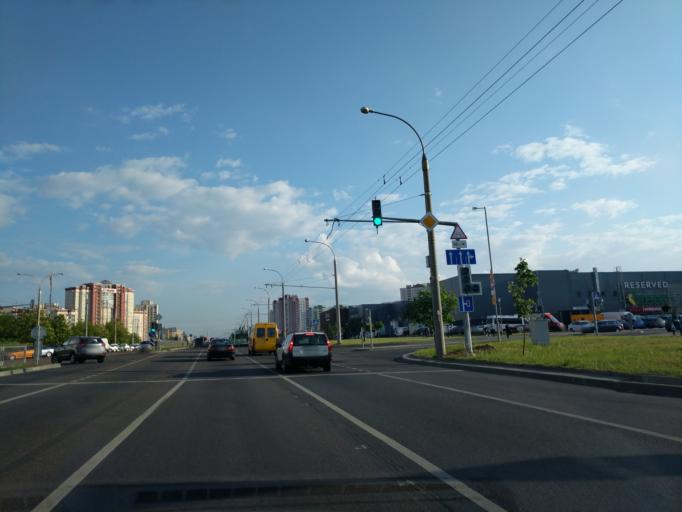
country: BY
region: Minsk
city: Novoye Medvezhino
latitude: 53.9101
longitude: 27.4360
